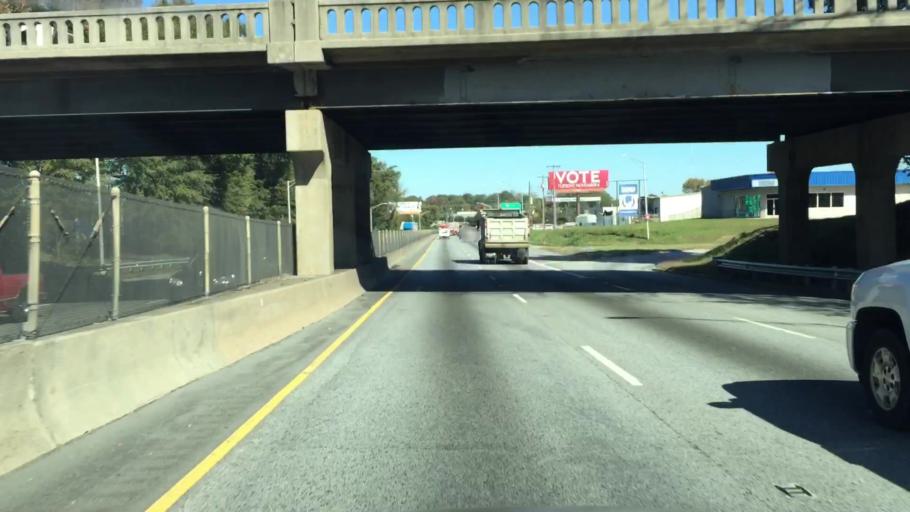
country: US
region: North Carolina
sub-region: Guilford County
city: Greensboro
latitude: 36.0798
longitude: -79.7671
